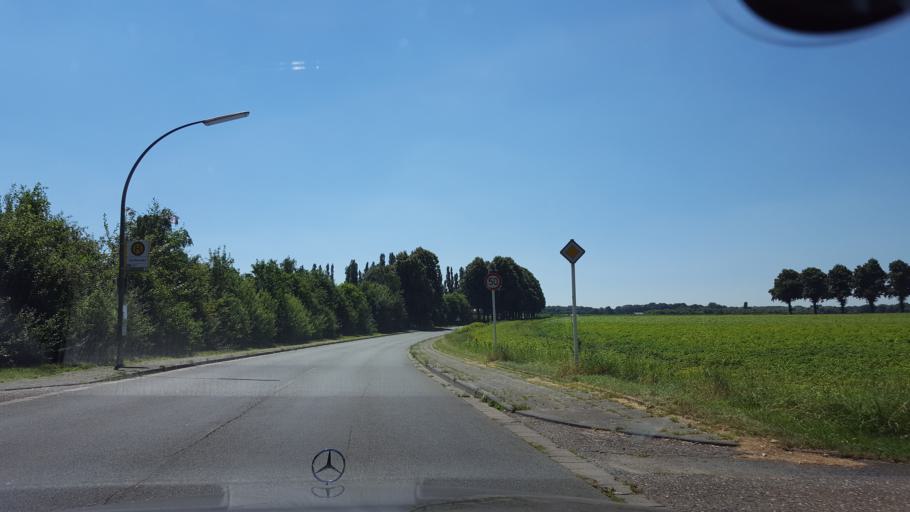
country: DE
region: North Rhine-Westphalia
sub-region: Regierungsbezirk Munster
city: Recklinghausen
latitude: 51.6520
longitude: 7.1577
